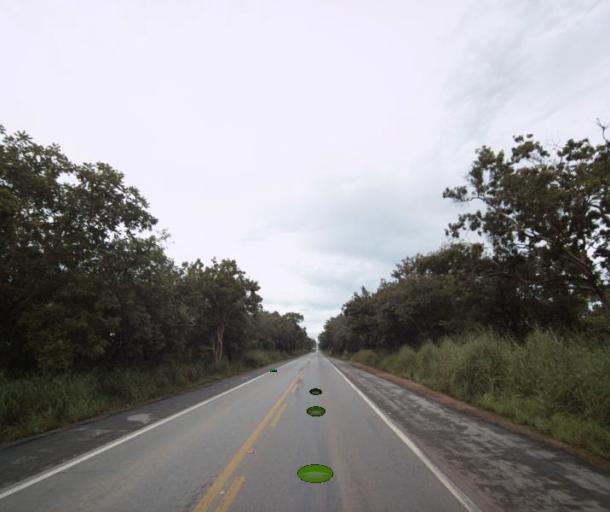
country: BR
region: Goias
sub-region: Porangatu
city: Porangatu
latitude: -13.4917
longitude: -49.1347
